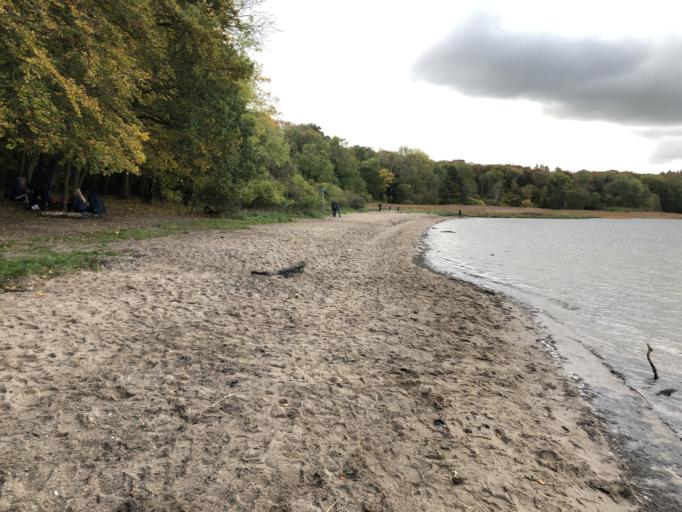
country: DK
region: Zealand
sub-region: Roskilde Kommune
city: Svogerslev
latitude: 55.6686
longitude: 12.0312
